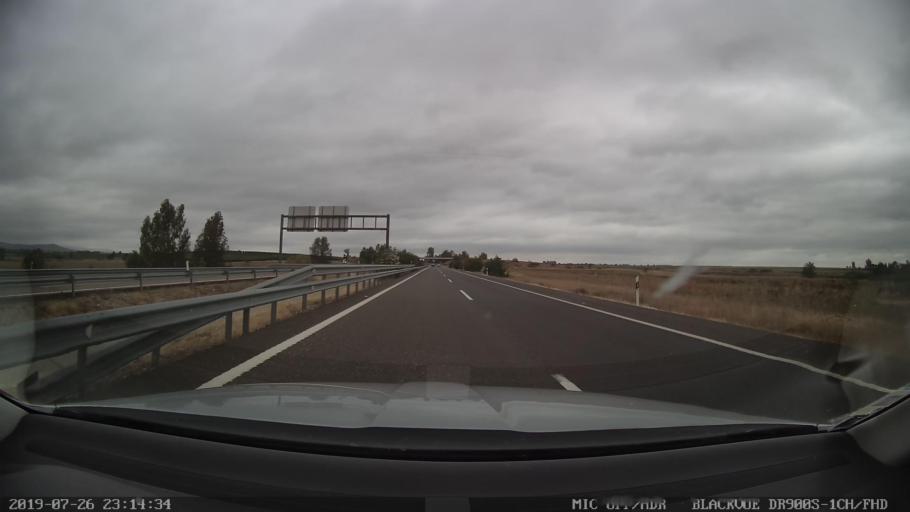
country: ES
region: Extremadura
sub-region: Provincia de Badajoz
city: Santa Amalia
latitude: 39.0394
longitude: -6.0643
